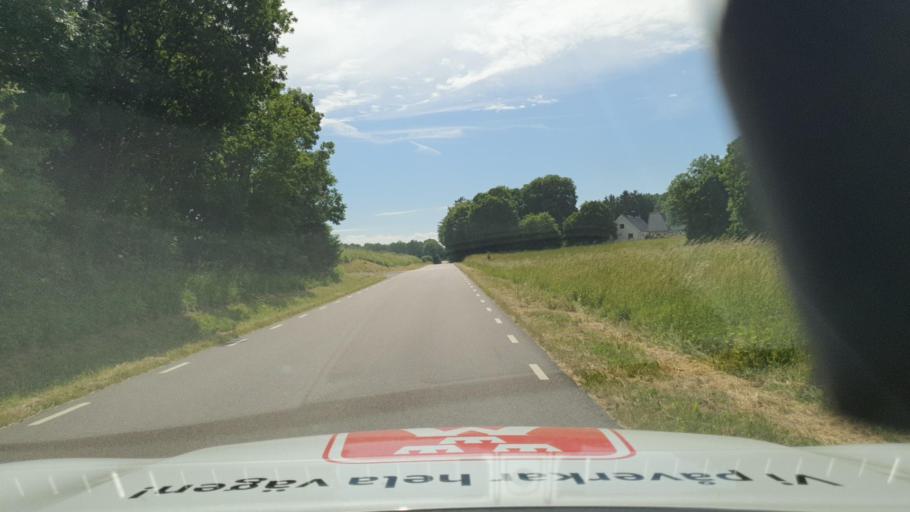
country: SE
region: Skane
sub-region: Tomelilla Kommun
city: Tomelilla
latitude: 55.6728
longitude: 13.9236
